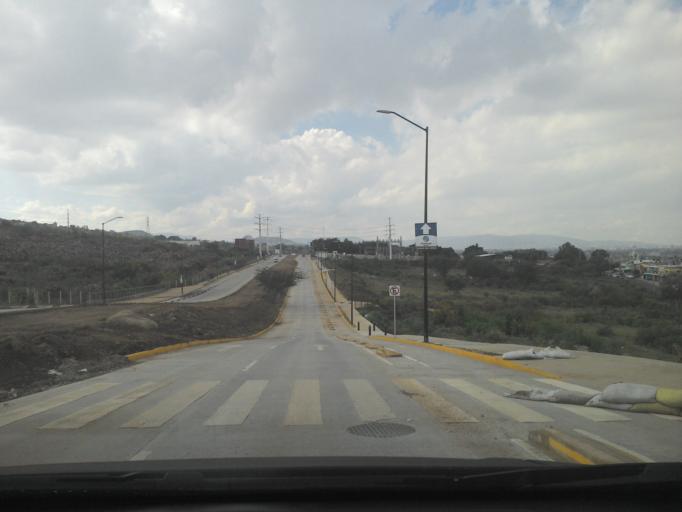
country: MX
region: Jalisco
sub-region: Tlajomulco de Zuniga
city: Altus Bosques
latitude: 20.6145
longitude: -103.3583
